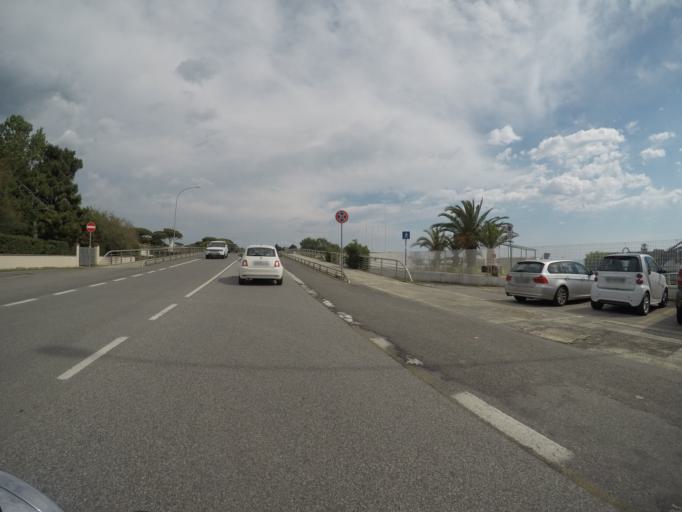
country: IT
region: Tuscany
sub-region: Provincia di Massa-Carrara
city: Capanne-Prato-Cinquale
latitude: 43.9790
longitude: 10.1422
